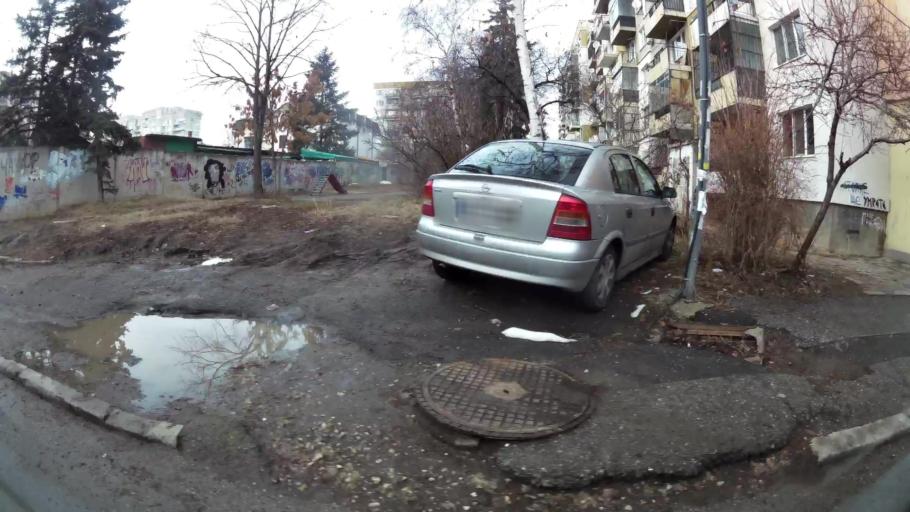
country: BG
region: Sofiya
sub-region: Obshtina Bozhurishte
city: Bozhurishte
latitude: 42.7183
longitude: 23.2478
